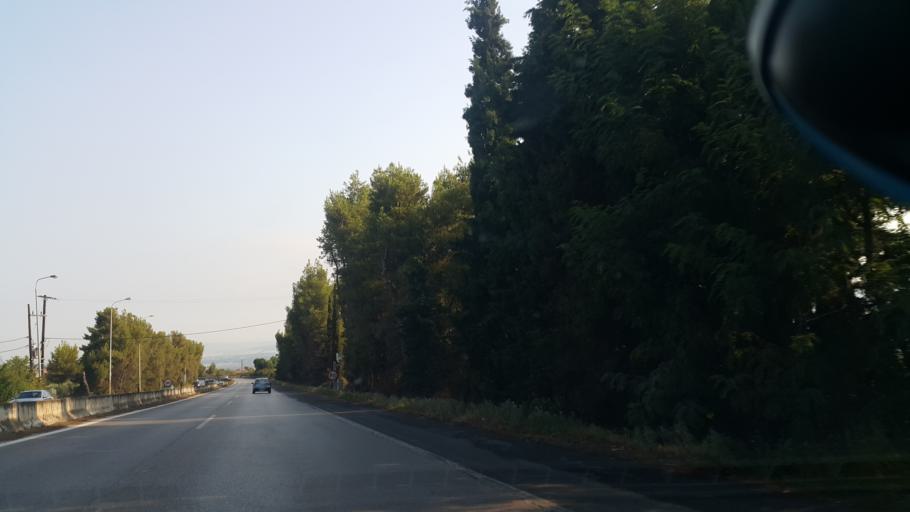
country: GR
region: Central Macedonia
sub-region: Nomos Thessalonikis
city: Kardia
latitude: 40.4629
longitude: 22.9981
